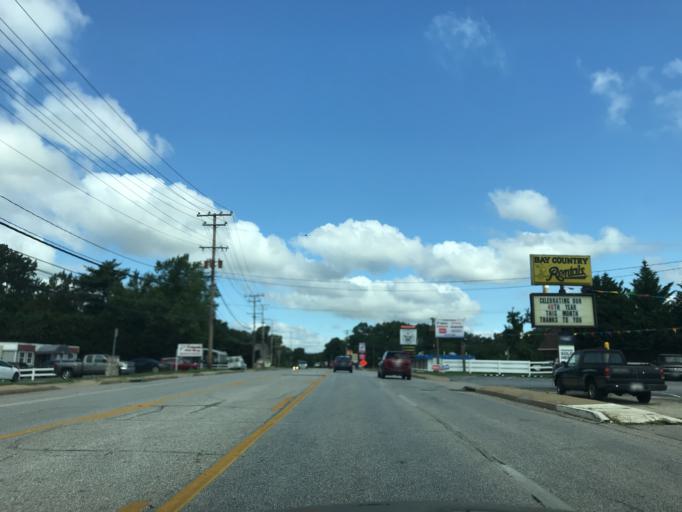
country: US
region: Maryland
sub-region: Anne Arundel County
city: Riviera Beach
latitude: 39.1692
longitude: -76.5323
